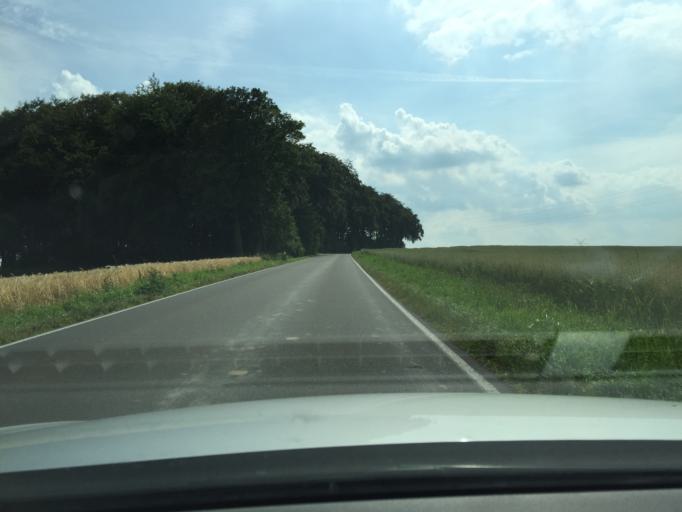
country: DE
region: North Rhine-Westphalia
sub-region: Regierungsbezirk Dusseldorf
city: Velbert
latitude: 51.3635
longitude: 7.1051
